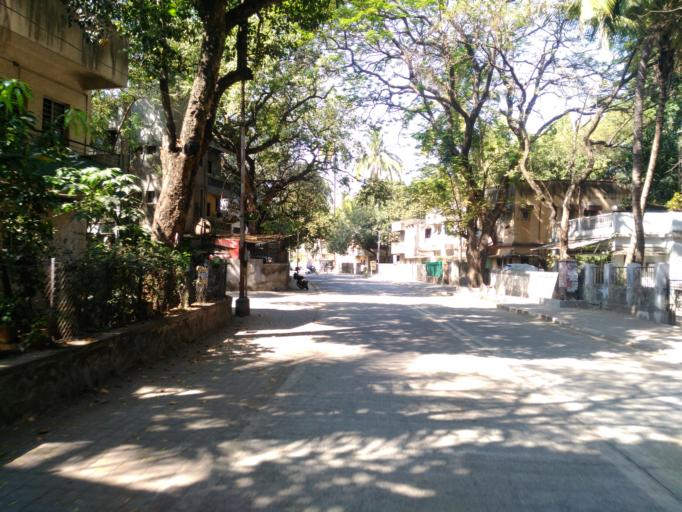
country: IN
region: Maharashtra
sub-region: Pune Division
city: Pune
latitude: 18.4809
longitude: 73.8530
